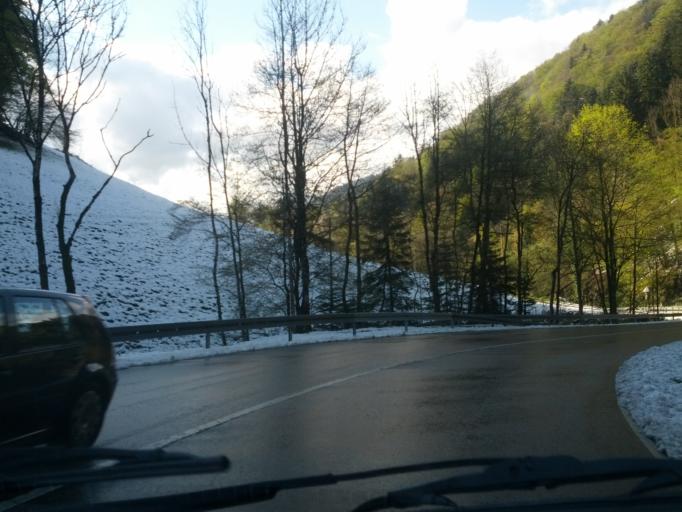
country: DE
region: Baden-Wuerttemberg
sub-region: Freiburg Region
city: Sankt Peter
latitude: 48.0229
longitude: 8.0212
